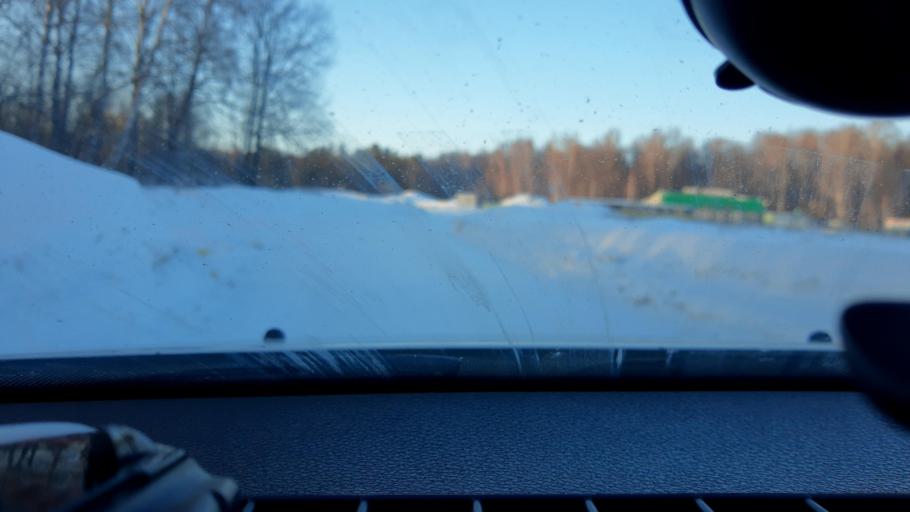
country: RU
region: Bashkortostan
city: Kudeyevskiy
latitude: 54.8121
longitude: 56.6760
